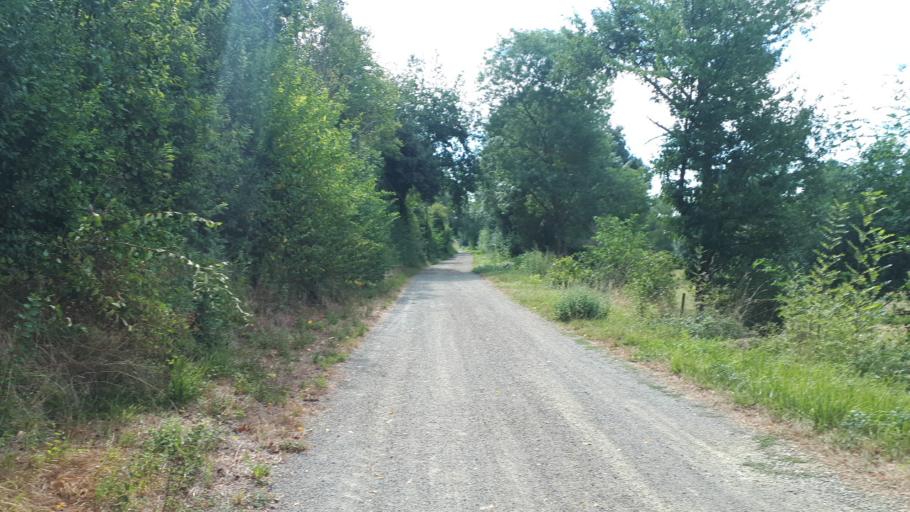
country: FR
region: Pays de la Loire
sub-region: Departement de Maine-et-Loire
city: Saint-Lambert-du-Lattay
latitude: 47.3235
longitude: -0.6560
